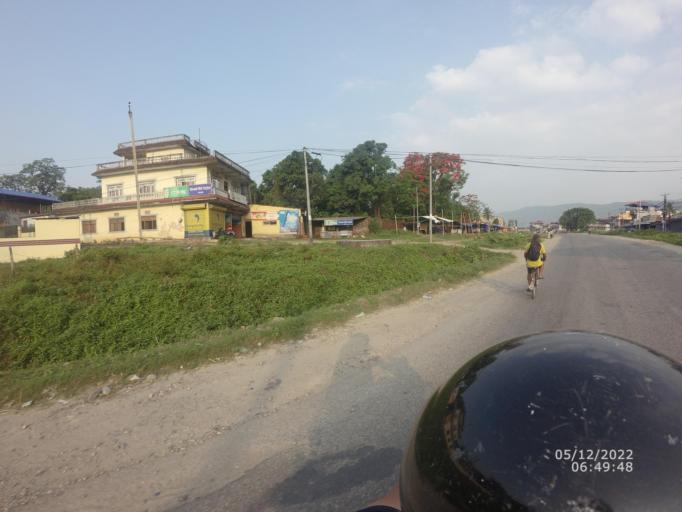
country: NP
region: Central Region
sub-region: Narayani Zone
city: Bharatpur
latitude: 27.7038
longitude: 84.4150
